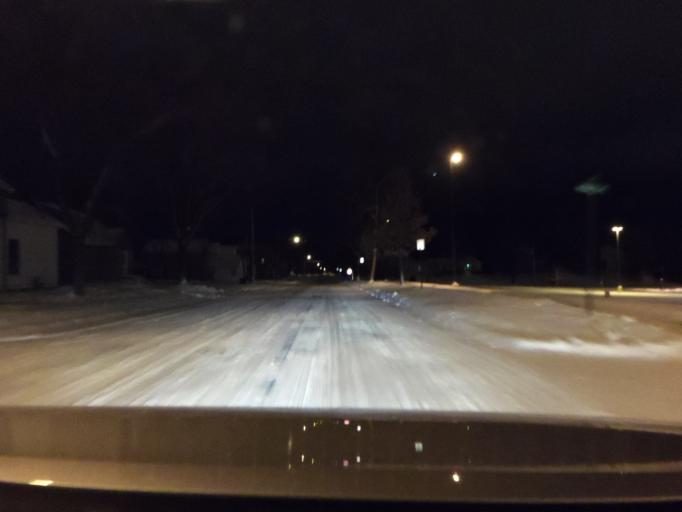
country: US
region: Wisconsin
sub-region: Dunn County
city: Menomonie
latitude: 44.8720
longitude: -91.9233
